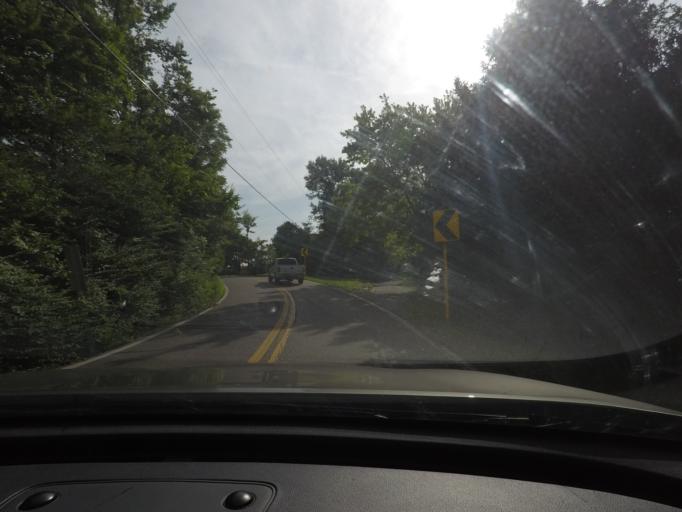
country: US
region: Missouri
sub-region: Saint Louis County
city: Town and Country
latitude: 38.6209
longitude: -90.4830
